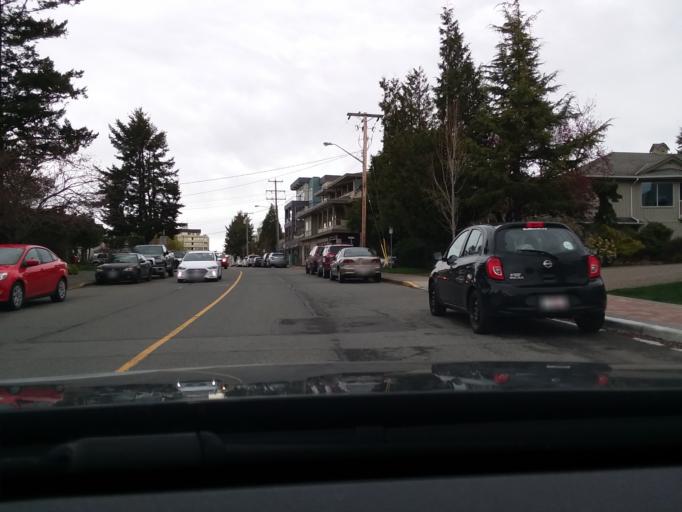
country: CA
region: British Columbia
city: North Saanich
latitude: 48.6463
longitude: -123.3954
